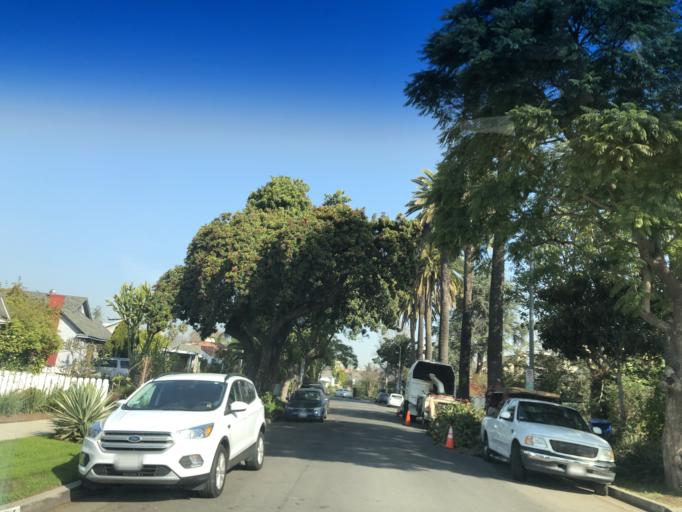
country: US
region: California
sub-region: Los Angeles County
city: Hollywood
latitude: 34.0534
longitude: -118.3172
